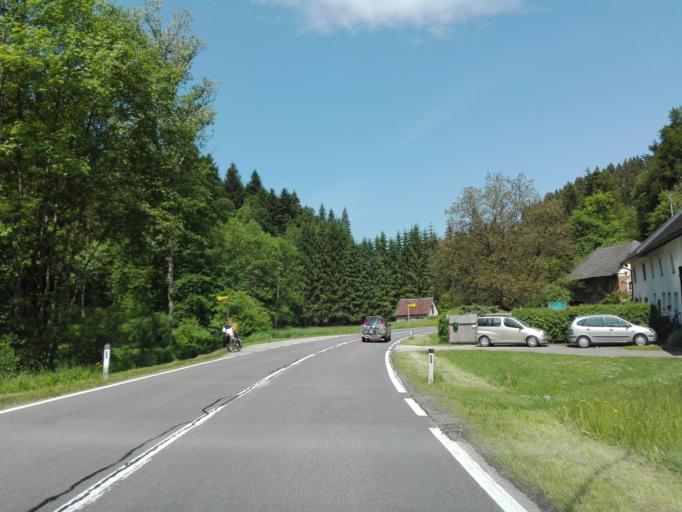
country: AT
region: Upper Austria
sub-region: Politischer Bezirk Rohrbach
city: Atzesberg
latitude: 48.4102
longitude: 13.8864
